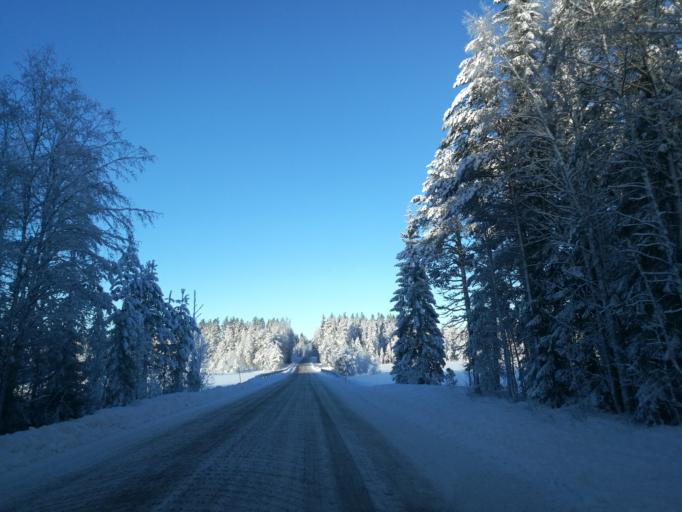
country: NO
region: Hedmark
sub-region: Grue
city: Kirkenaer
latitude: 60.5451
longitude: 12.5450
